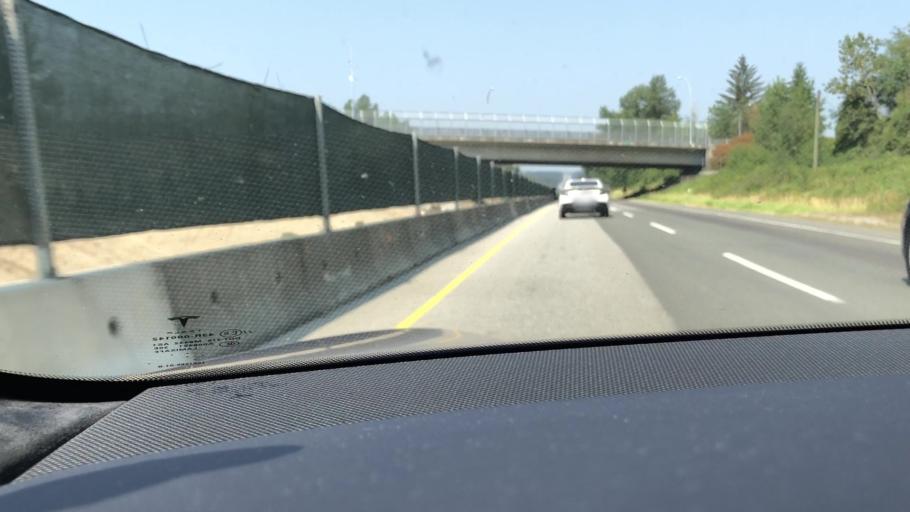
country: CA
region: British Columbia
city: Walnut Grove
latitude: 49.1580
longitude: -122.6441
